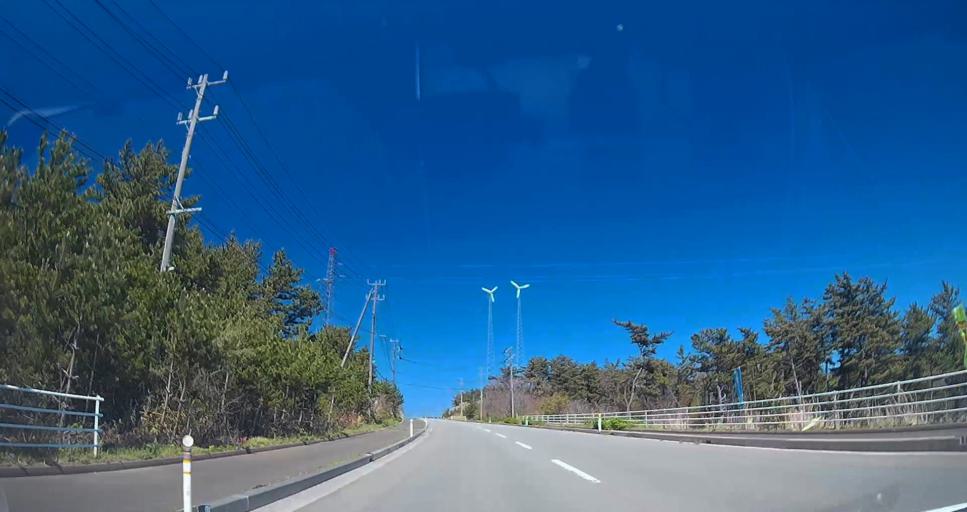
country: JP
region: Hokkaido
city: Hakodate
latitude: 41.5058
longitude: 140.9151
